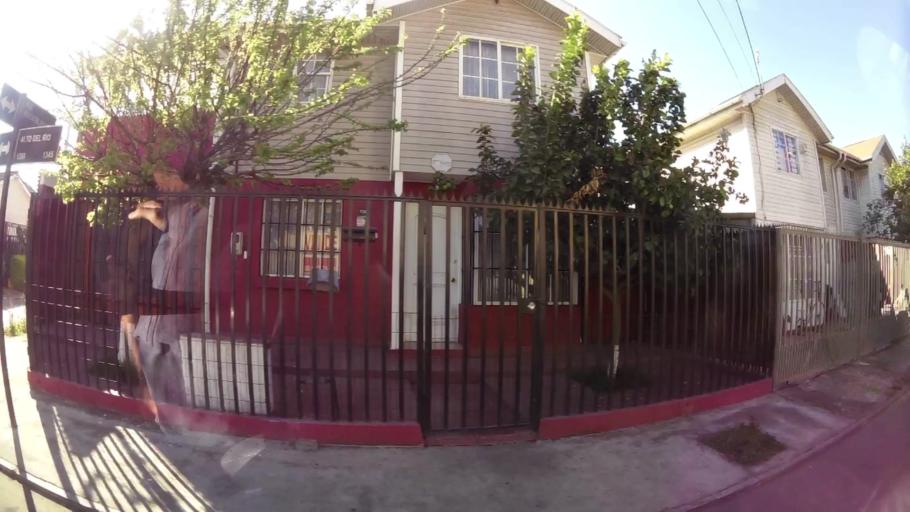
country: CL
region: Santiago Metropolitan
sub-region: Provincia de Santiago
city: Lo Prado
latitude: -33.4912
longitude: -70.7850
